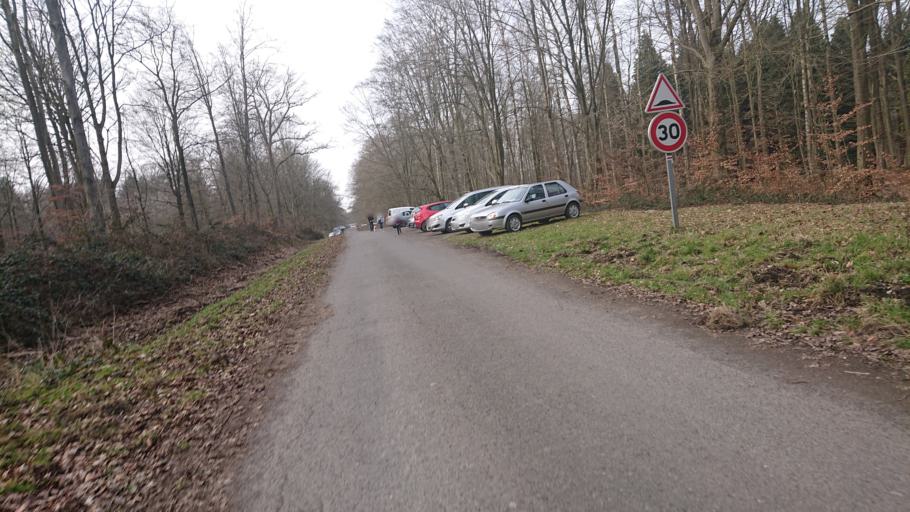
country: FR
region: Nord-Pas-de-Calais
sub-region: Departement du Nord
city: Landrecies
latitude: 50.1662
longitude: 3.7042
